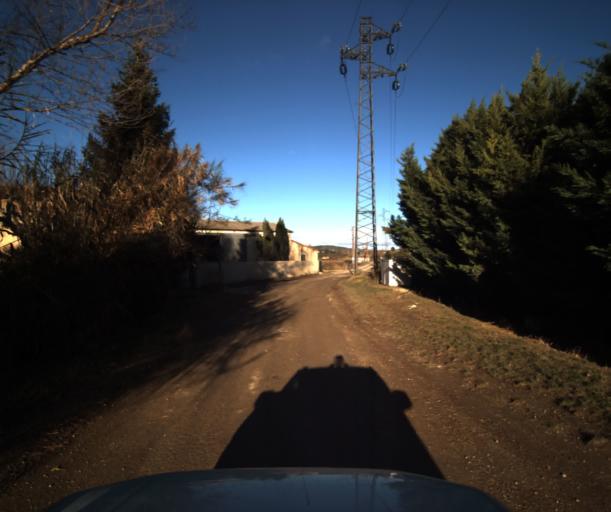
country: FR
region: Provence-Alpes-Cote d'Azur
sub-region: Departement du Vaucluse
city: Pertuis
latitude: 43.6840
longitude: 5.4715
